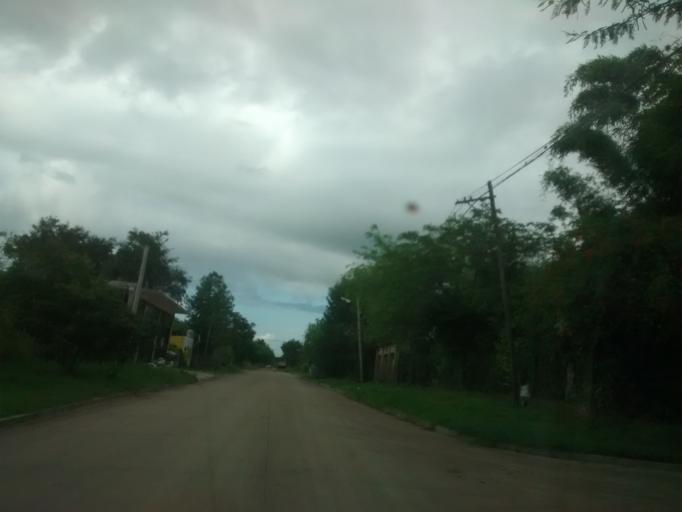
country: AR
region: Chaco
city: Puerto Tirol
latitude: -27.3814
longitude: -59.0854
